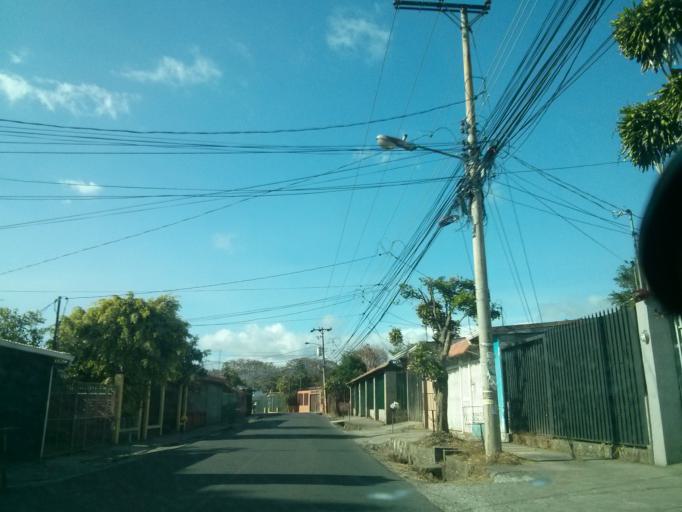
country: CR
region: San Jose
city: Sabanilla
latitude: 9.9407
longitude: -84.0425
